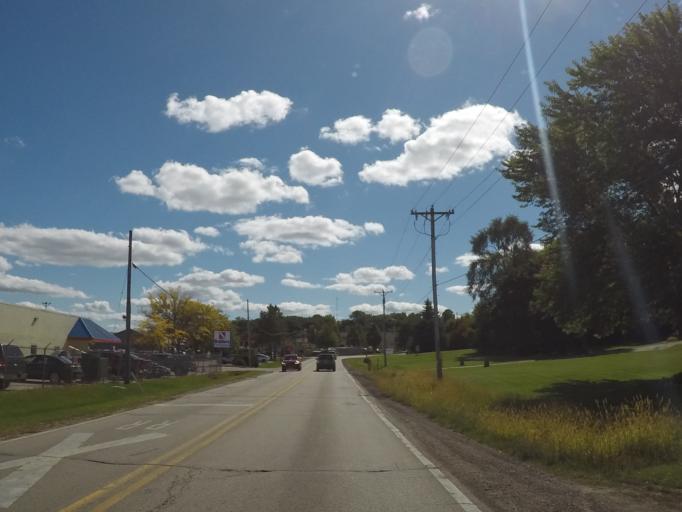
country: US
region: Wisconsin
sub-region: Dane County
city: Middleton
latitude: 43.0959
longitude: -89.5351
